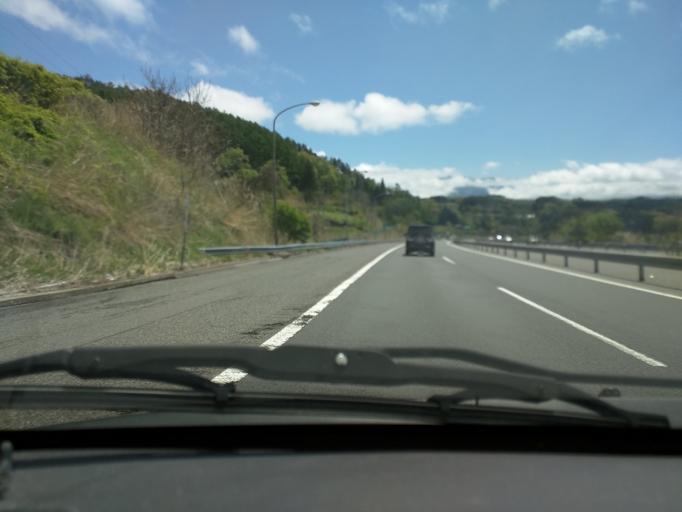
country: JP
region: Nagano
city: Iiyama
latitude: 36.8031
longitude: 138.3122
